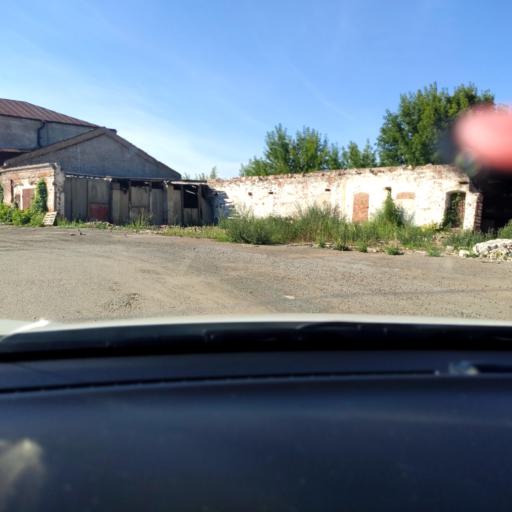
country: RU
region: Tatarstan
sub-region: Gorod Kazan'
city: Kazan
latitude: 55.8049
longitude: 49.0653
